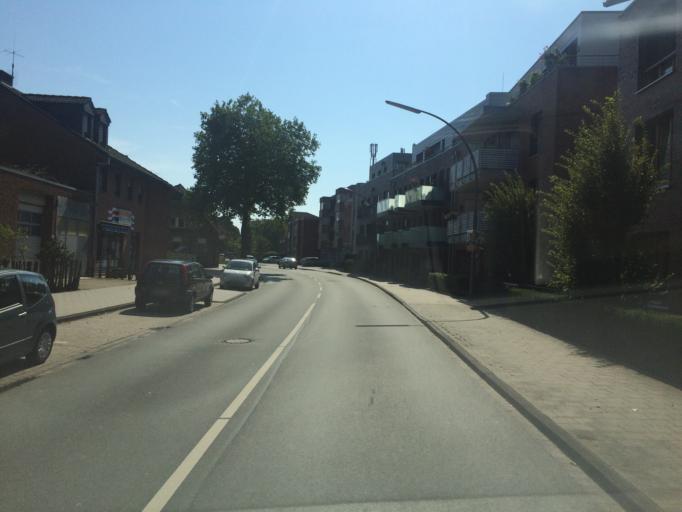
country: DE
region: North Rhine-Westphalia
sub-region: Regierungsbezirk Munster
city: Muenster
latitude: 51.9862
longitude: 7.6993
